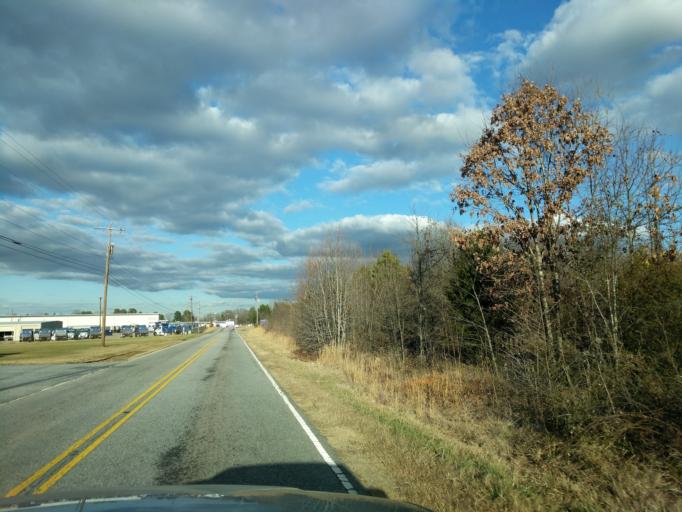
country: US
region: South Carolina
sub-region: Spartanburg County
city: Duncan
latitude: 34.8869
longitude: -82.1478
